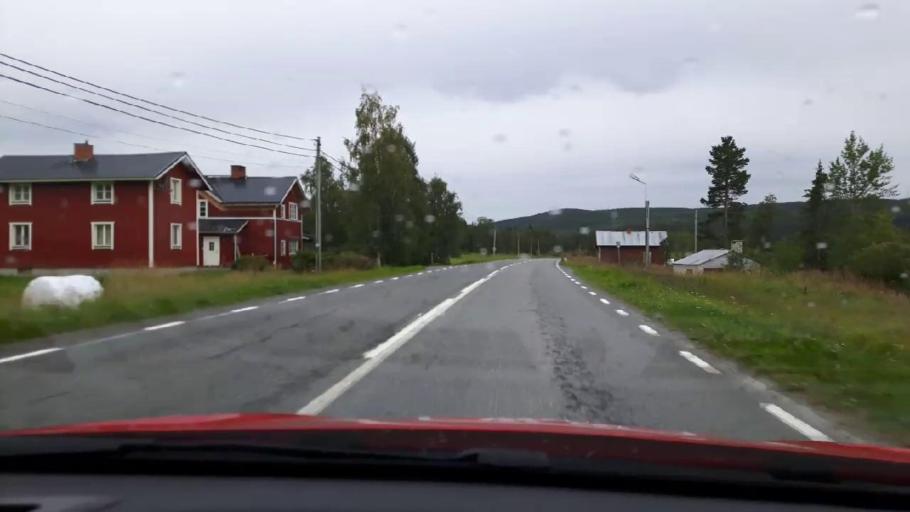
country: SE
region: Jaemtland
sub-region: Are Kommun
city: Jarpen
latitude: 63.4059
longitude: 13.3697
